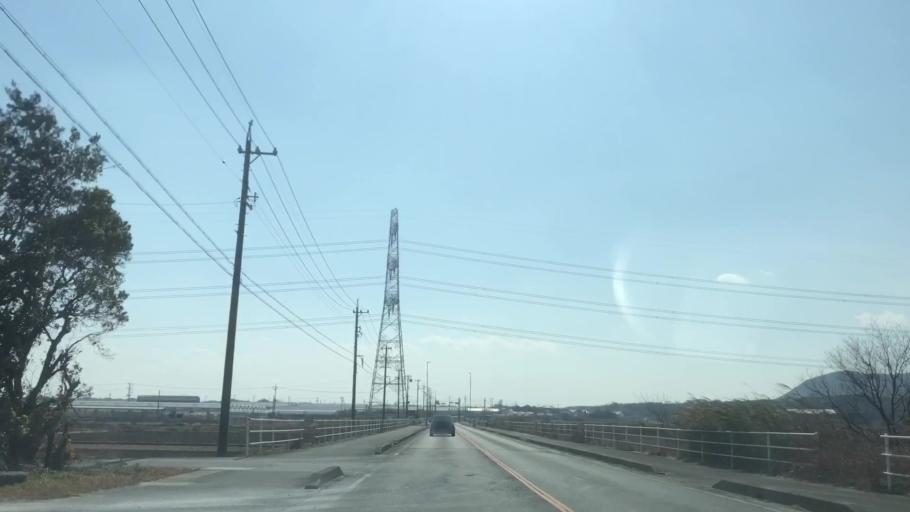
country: JP
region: Aichi
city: Tahara
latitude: 34.6418
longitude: 137.2391
